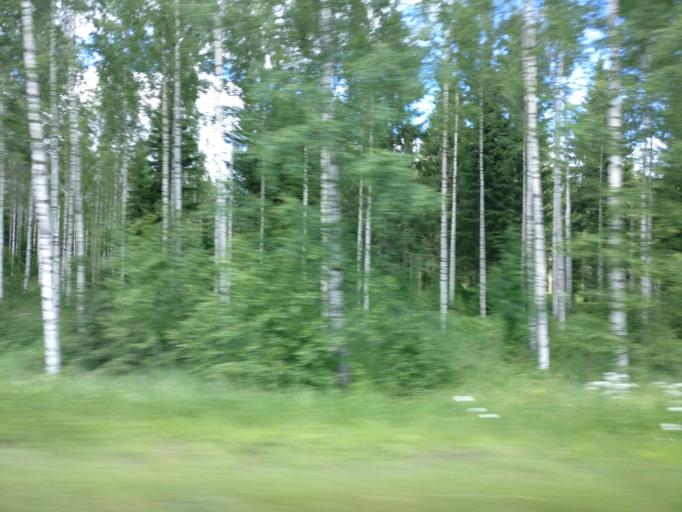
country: FI
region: Southern Savonia
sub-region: Savonlinna
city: Kerimaeki
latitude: 61.8474
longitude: 29.1819
